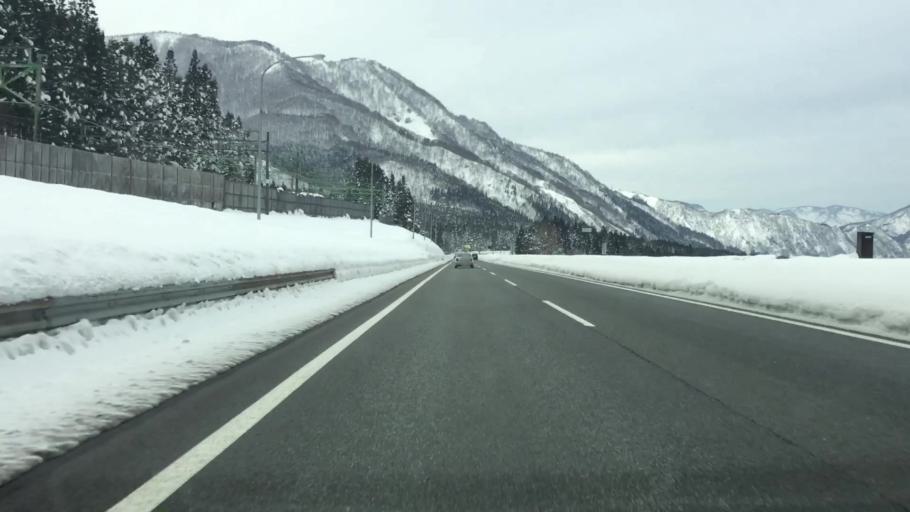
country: JP
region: Niigata
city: Shiozawa
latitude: 36.8764
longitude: 138.8608
